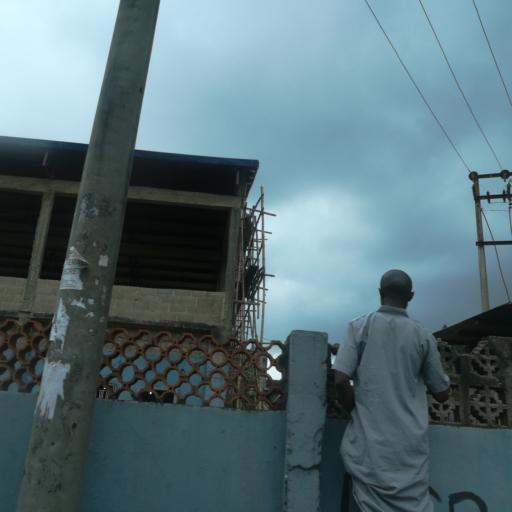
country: NG
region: Lagos
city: Agege
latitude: 6.6104
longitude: 3.3013
